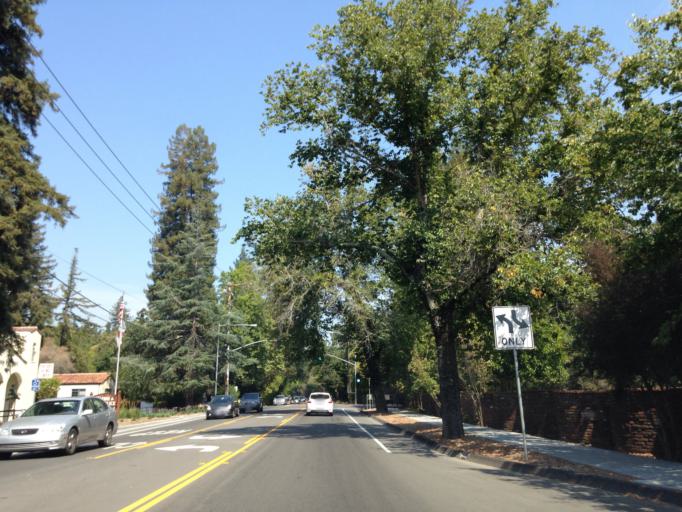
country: US
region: California
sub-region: Marin County
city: Ross
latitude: 37.9628
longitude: -122.5559
